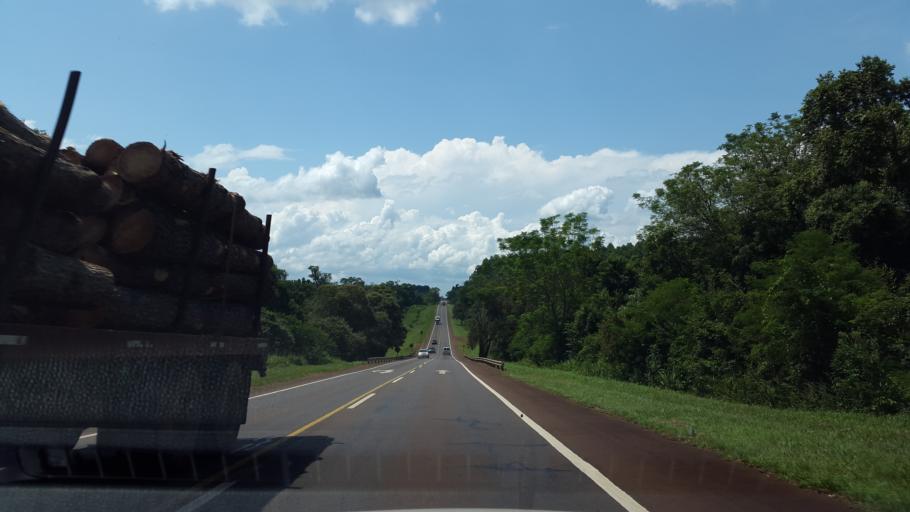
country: AR
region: Misiones
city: El Alcazar
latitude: -26.7089
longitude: -54.8461
